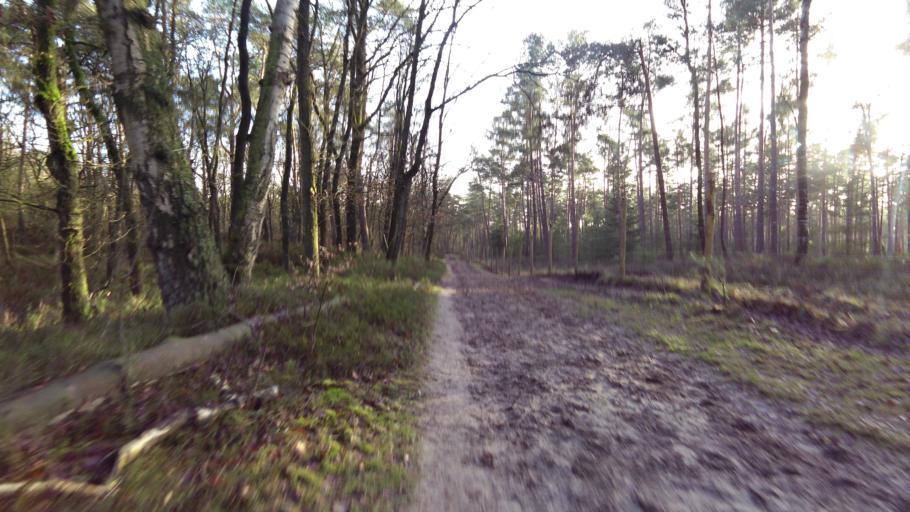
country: NL
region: Gelderland
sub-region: Gemeente Epe
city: Vaassen
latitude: 52.2597
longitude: 5.9177
